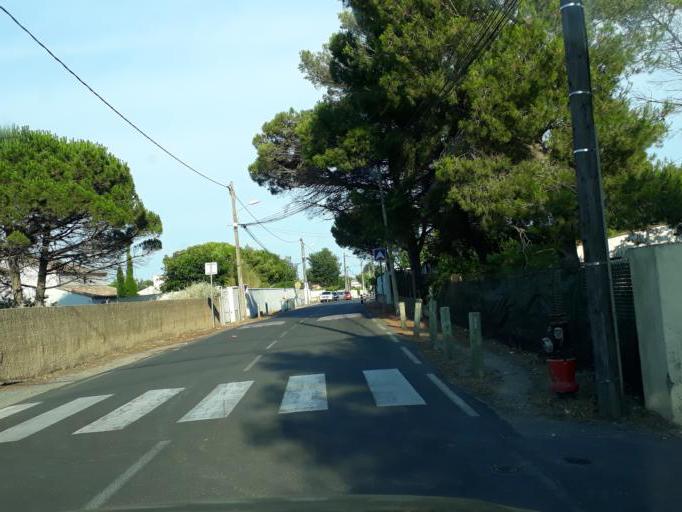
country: FR
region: Languedoc-Roussillon
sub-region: Departement de l'Herault
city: Agde
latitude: 43.2804
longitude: 3.4608
